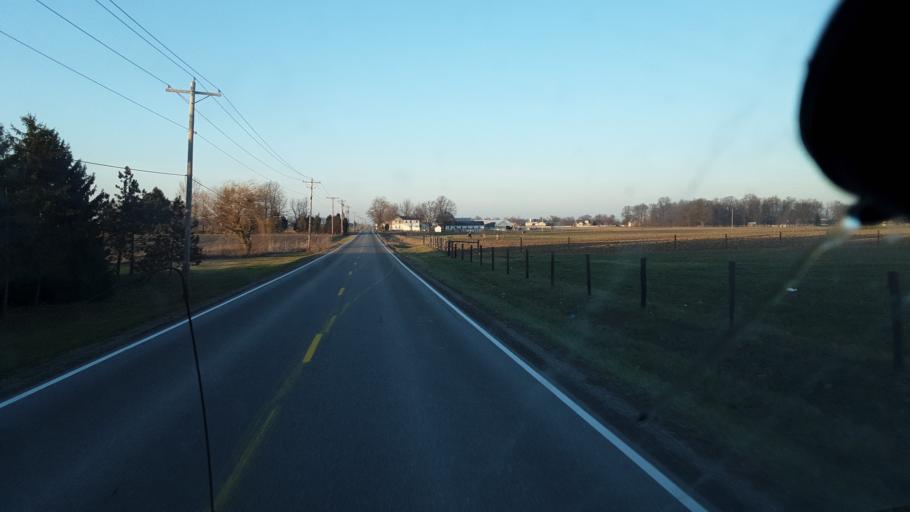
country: US
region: Indiana
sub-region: Allen County
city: Harlan
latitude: 41.1927
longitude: -84.9412
